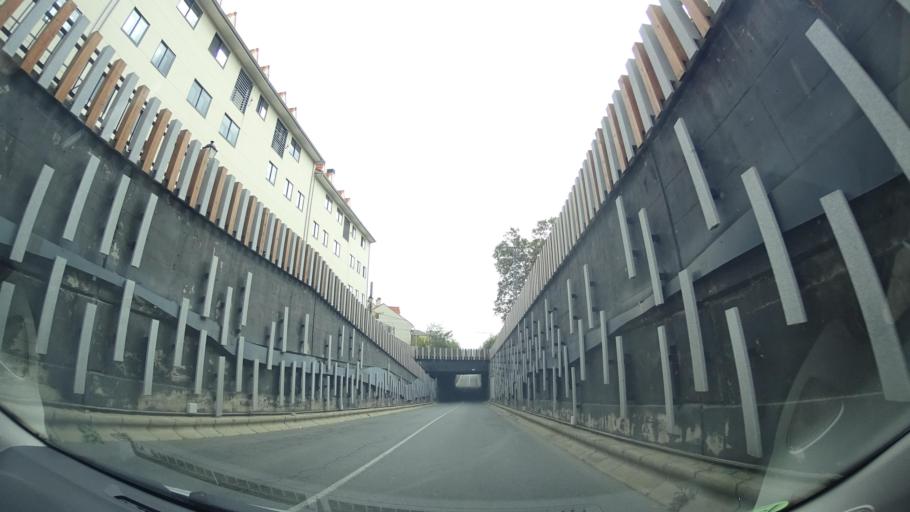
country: ES
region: Madrid
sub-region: Provincia de Madrid
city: El Escorial
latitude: 40.5845
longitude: -4.1330
